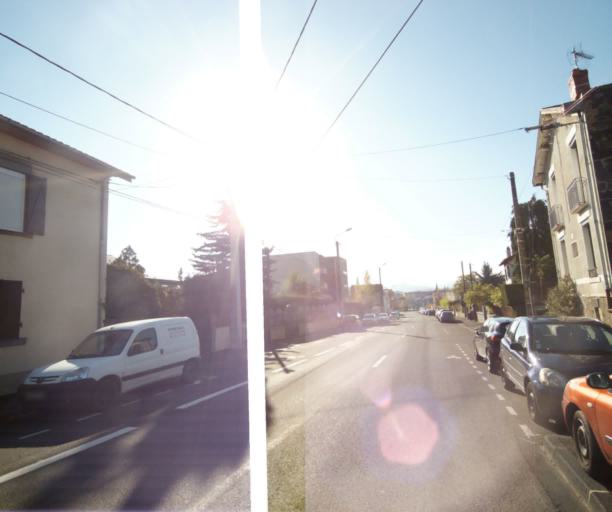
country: FR
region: Auvergne
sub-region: Departement du Puy-de-Dome
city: Clermont-Ferrand
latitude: 45.7921
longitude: 3.0841
